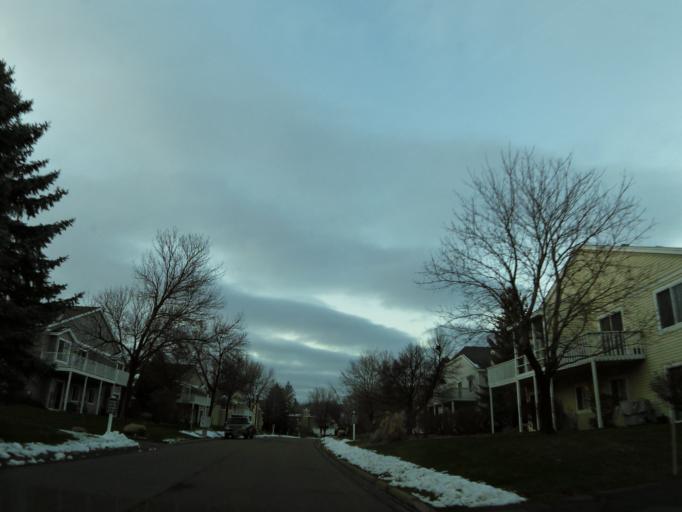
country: US
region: Minnesota
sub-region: Hennepin County
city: Minnetonka Mills
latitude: 44.9024
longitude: -93.4255
